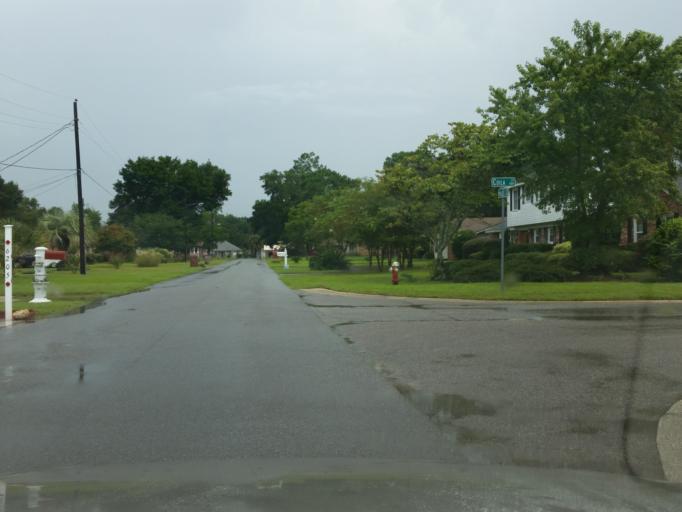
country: US
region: Florida
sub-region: Escambia County
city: Ferry Pass
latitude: 30.4999
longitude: -87.1954
